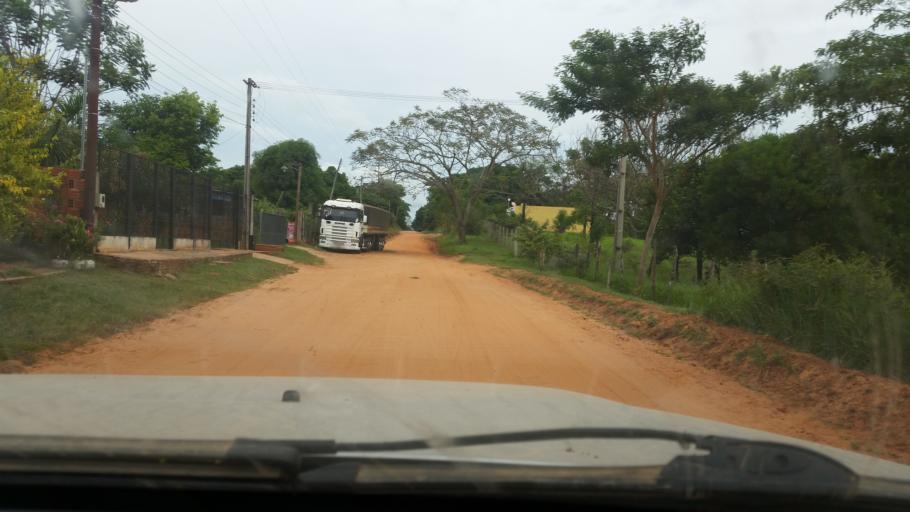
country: PY
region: Guaira
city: Independencia
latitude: -25.7066
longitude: -56.1900
